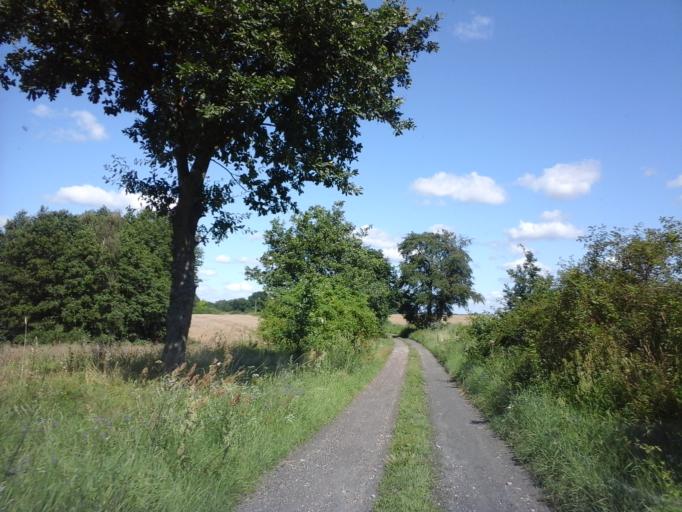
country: PL
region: West Pomeranian Voivodeship
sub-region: Powiat choszczenski
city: Recz
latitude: 53.2299
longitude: 15.5690
